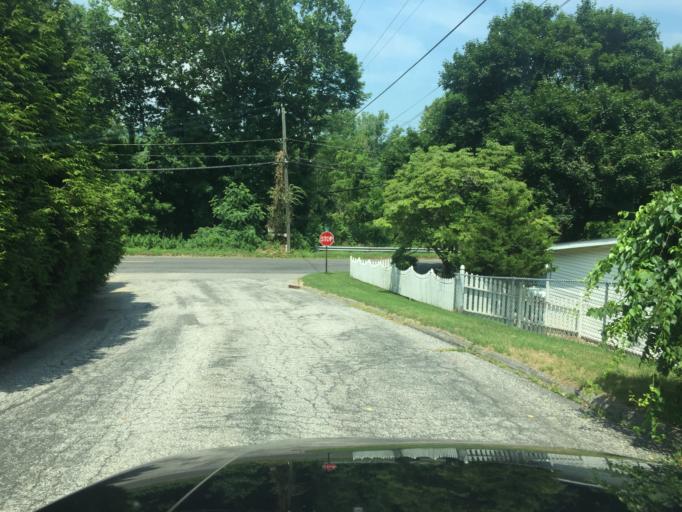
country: US
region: Connecticut
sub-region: Litchfield County
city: New Milford
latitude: 41.5404
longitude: -73.4110
